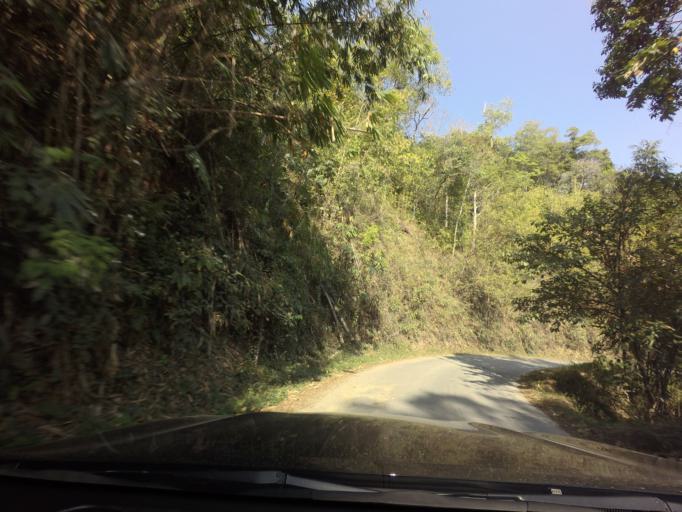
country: TH
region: Kanchanaburi
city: Thong Pha Phum
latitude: 14.7000
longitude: 98.4581
